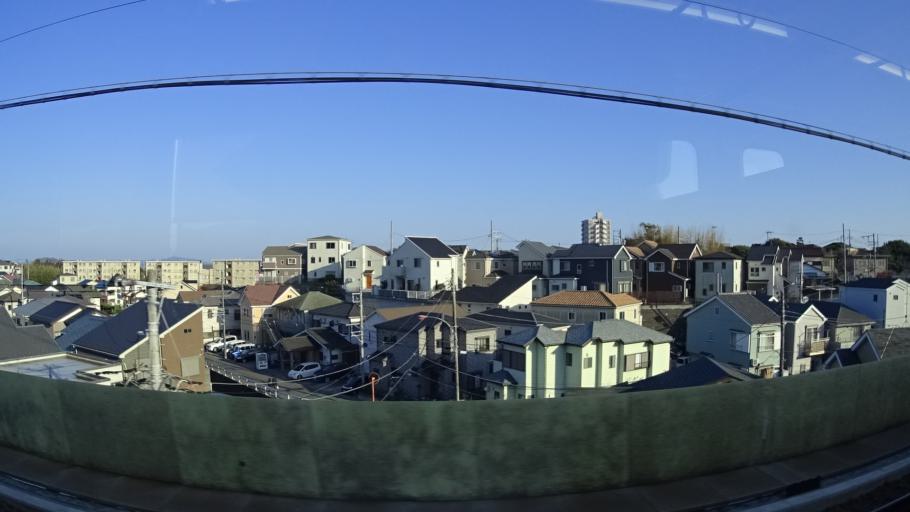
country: JP
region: Kanagawa
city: Miura
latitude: 35.2005
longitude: 139.6675
